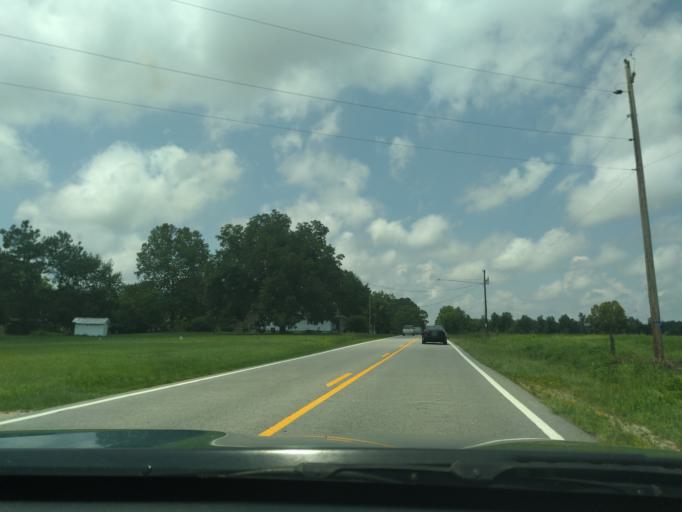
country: US
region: North Carolina
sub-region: Nash County
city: Red Oak
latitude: 36.0060
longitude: -77.8473
